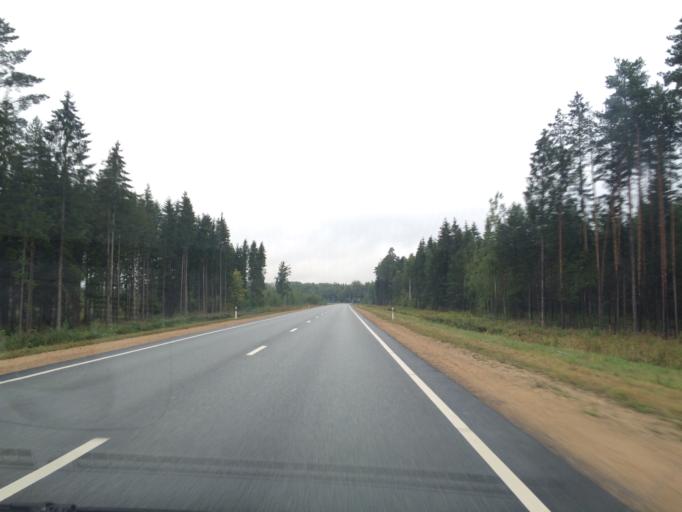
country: LV
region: Ogre
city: Ogre
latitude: 56.8546
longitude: 24.6502
